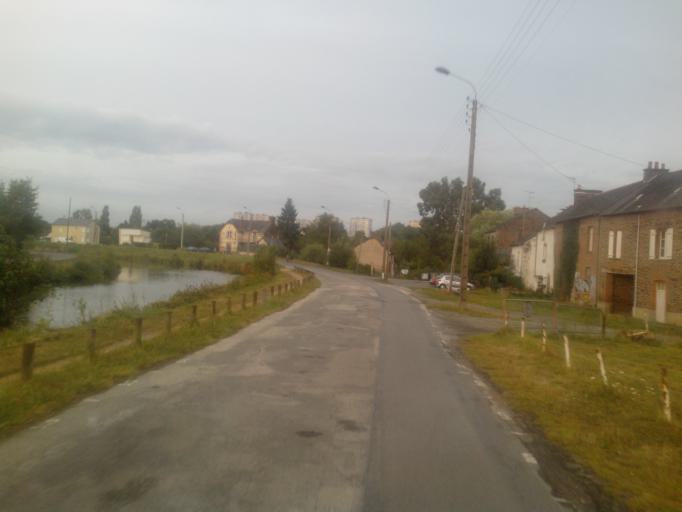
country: FR
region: Brittany
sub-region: Departement d'Ille-et-Vilaine
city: Rennes
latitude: 48.1234
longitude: -1.6766
